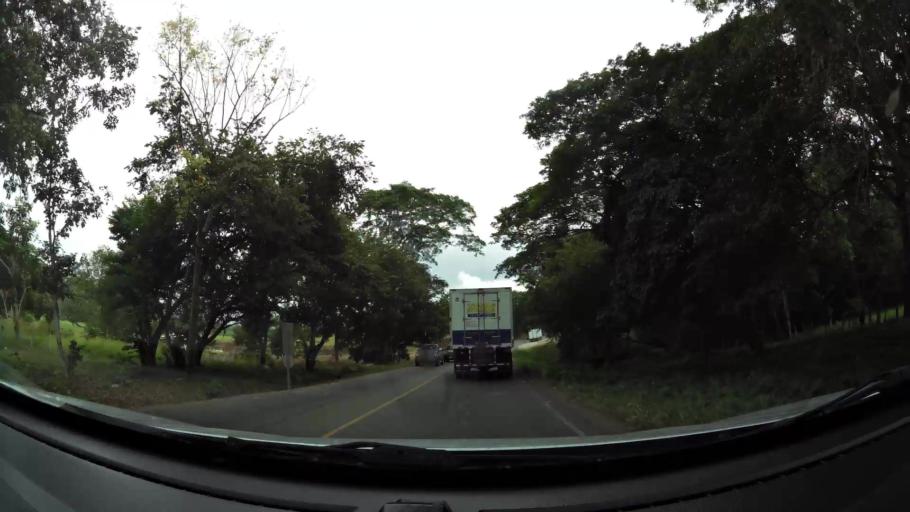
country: CR
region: Guanacaste
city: Juntas
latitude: 10.1715
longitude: -84.9229
